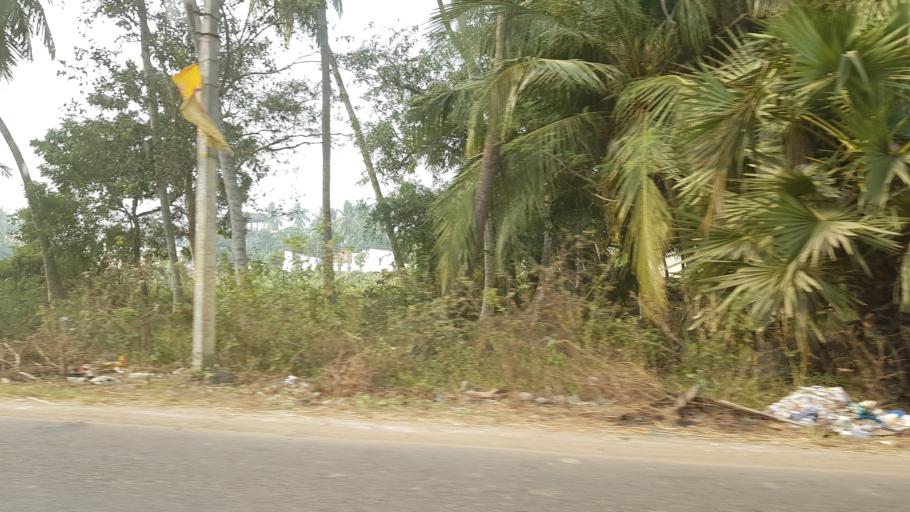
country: IN
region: Andhra Pradesh
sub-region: West Godavari
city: Akividu
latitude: 16.5284
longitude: 81.3867
